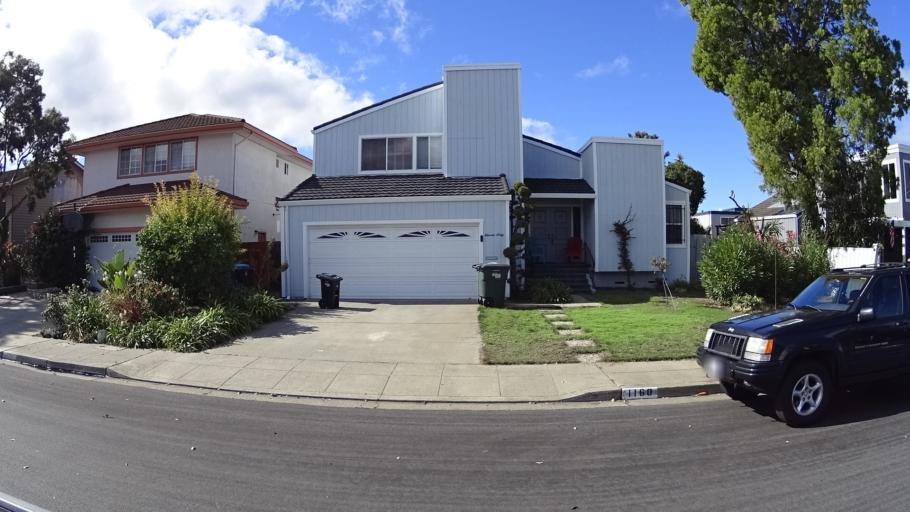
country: US
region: California
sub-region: San Mateo County
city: Foster City
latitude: 37.5599
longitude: -122.2541
